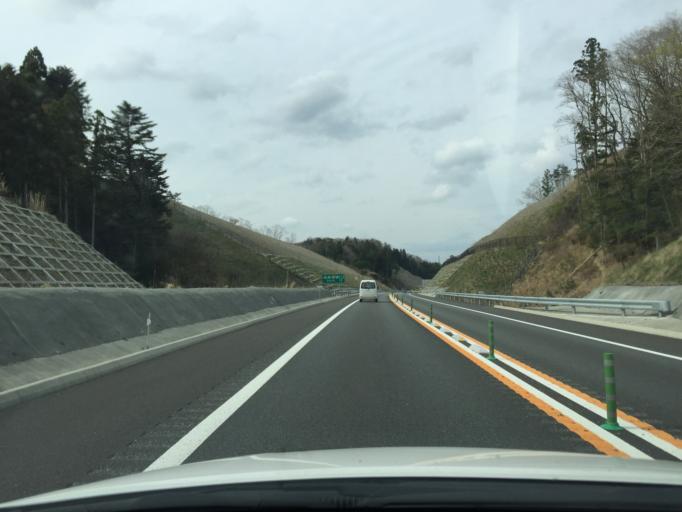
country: JP
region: Fukushima
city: Namie
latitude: 37.6429
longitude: 140.9175
